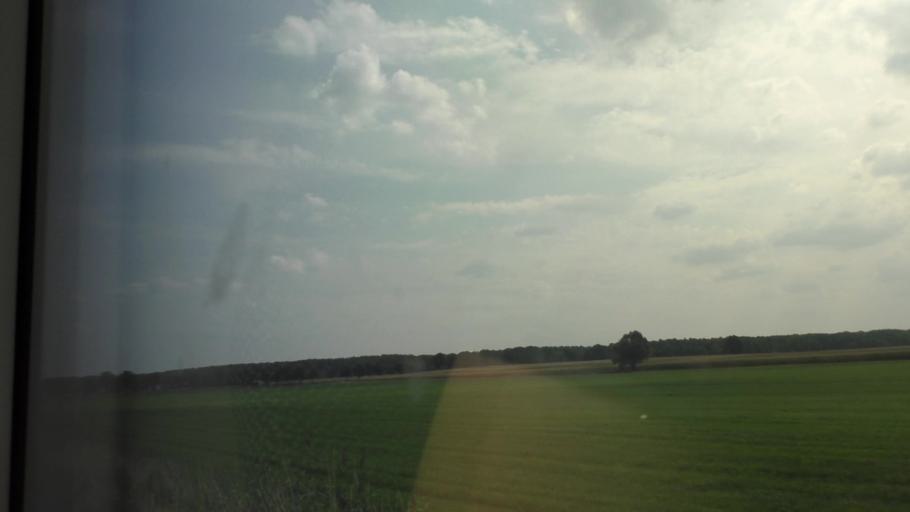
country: DE
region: Brandenburg
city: Beeskow
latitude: 52.1663
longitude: 14.3223
